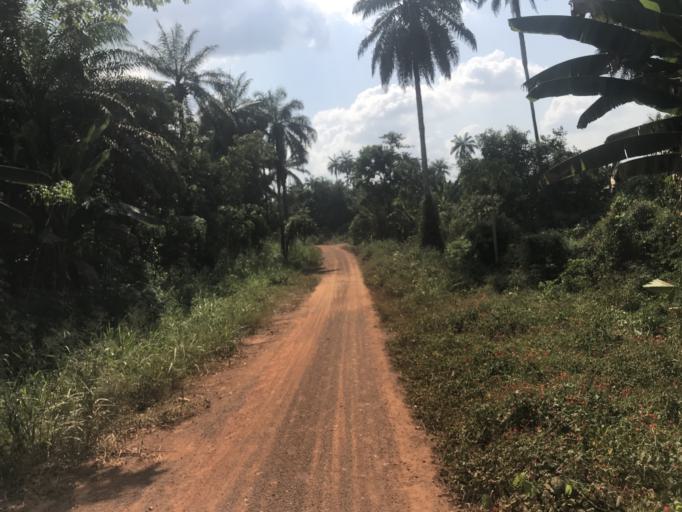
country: NG
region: Osun
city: Ibokun
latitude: 7.8102
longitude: 4.6939
